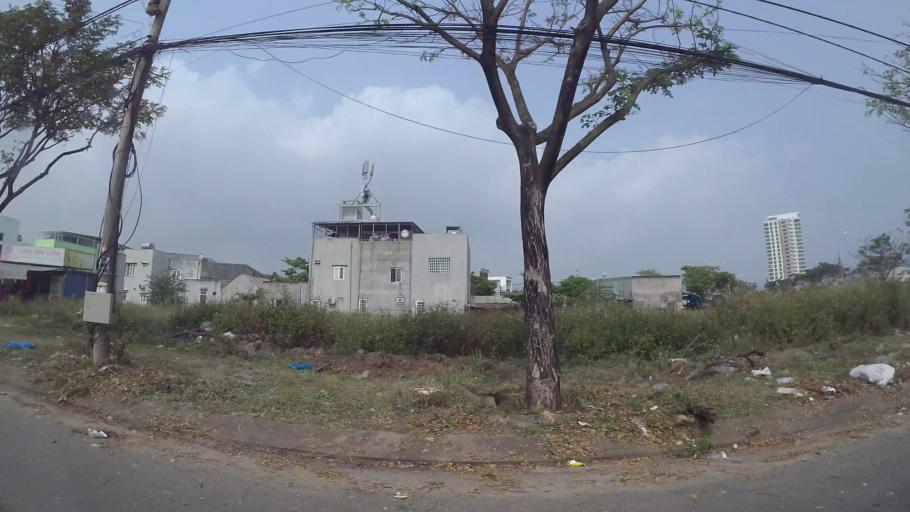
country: VN
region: Da Nang
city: Da Nang
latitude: 16.0974
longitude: 108.2338
